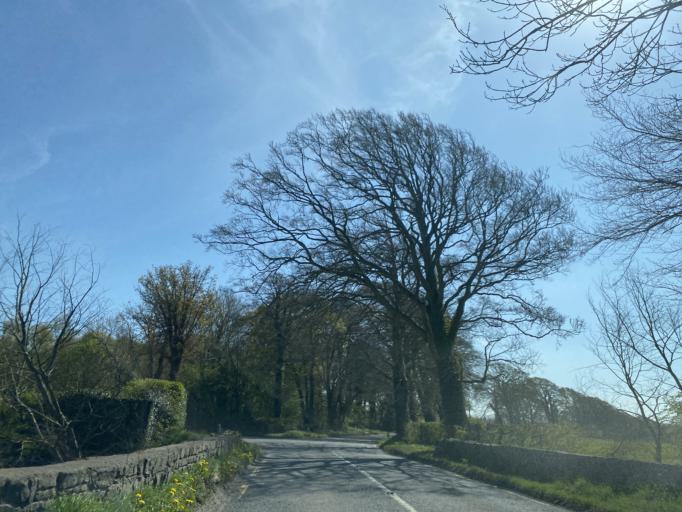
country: IE
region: Leinster
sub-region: Kildare
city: Kill
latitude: 53.3021
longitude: -6.6111
